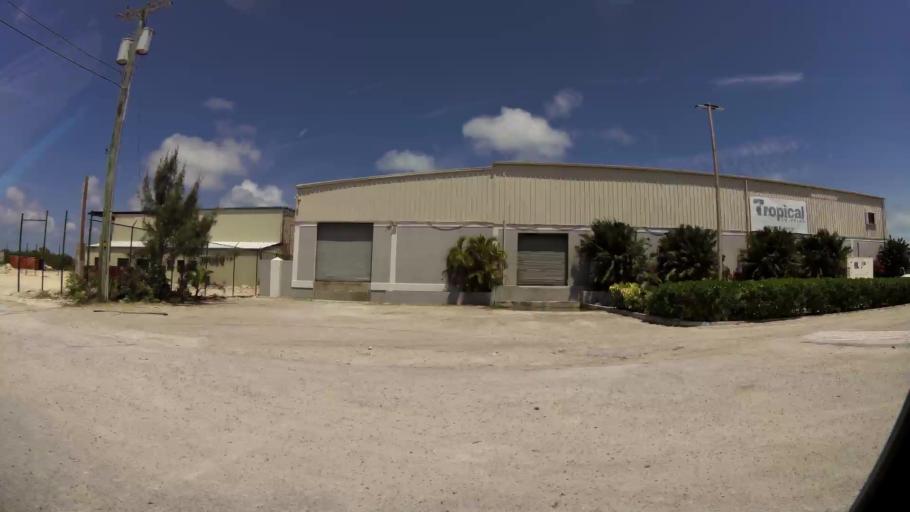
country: BS
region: Mayaguana
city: Abraham's Bay
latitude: 21.7710
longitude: -72.2560
